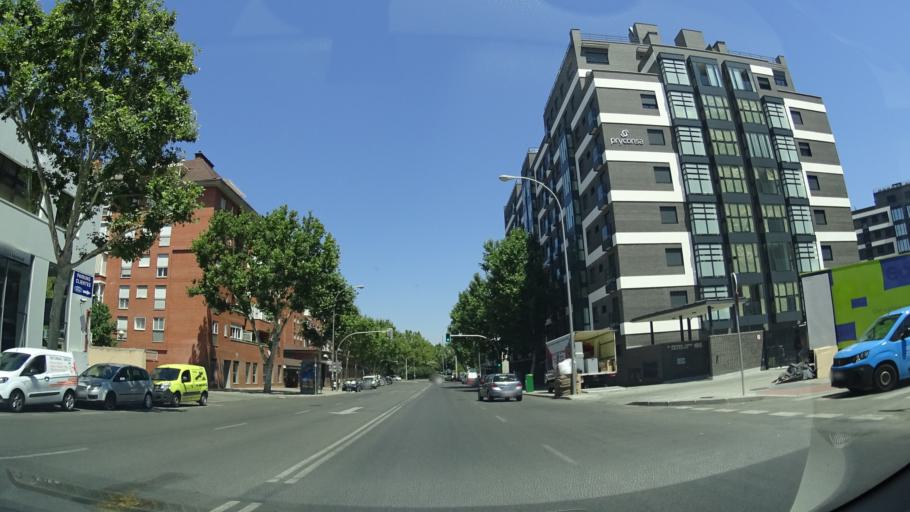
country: ES
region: Madrid
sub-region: Provincia de Madrid
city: Usera
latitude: 40.3837
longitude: -3.6958
